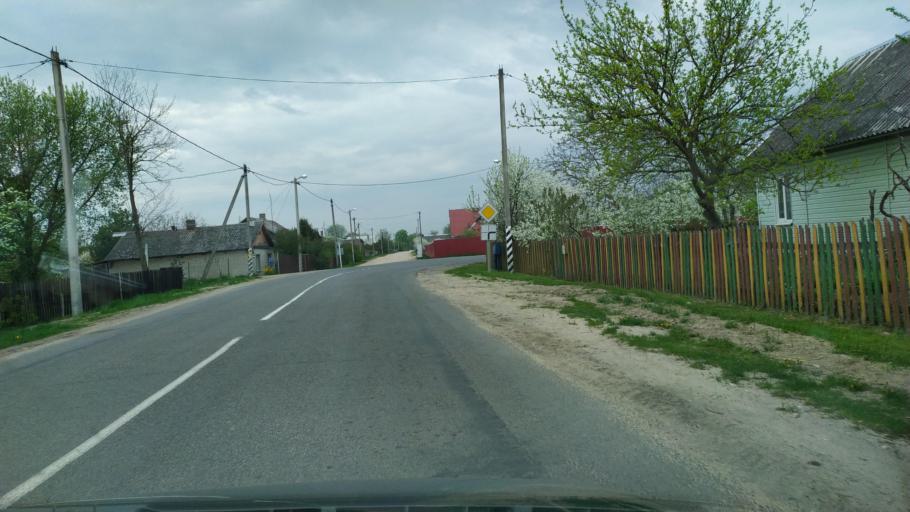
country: BY
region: Brest
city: Zhabinka
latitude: 52.1572
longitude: 24.0852
